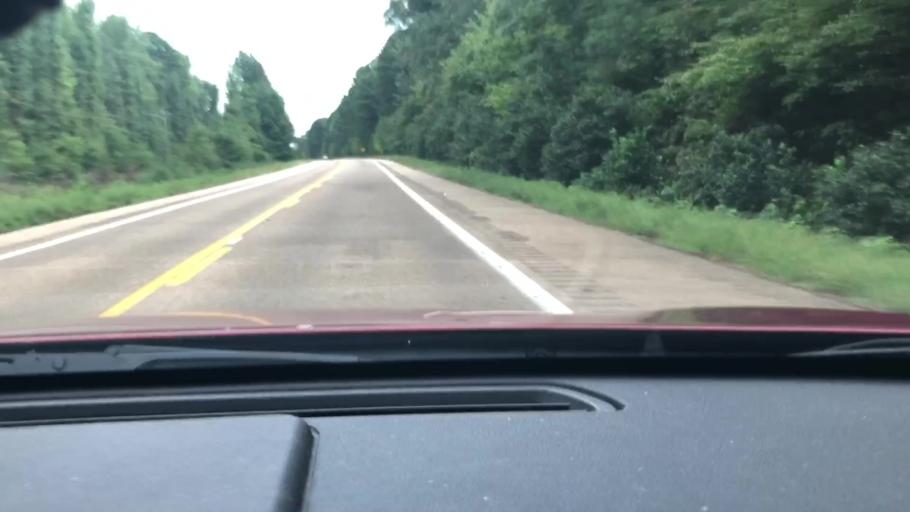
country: US
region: Arkansas
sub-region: Miller County
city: Texarkana
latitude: 33.4193
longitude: -93.8348
